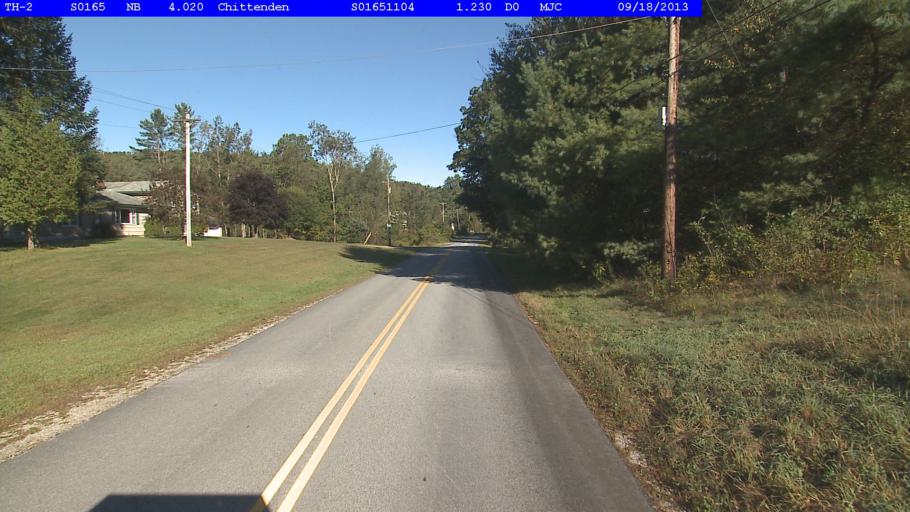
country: US
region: Vermont
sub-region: Rutland County
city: Rutland
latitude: 43.6941
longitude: -72.9550
